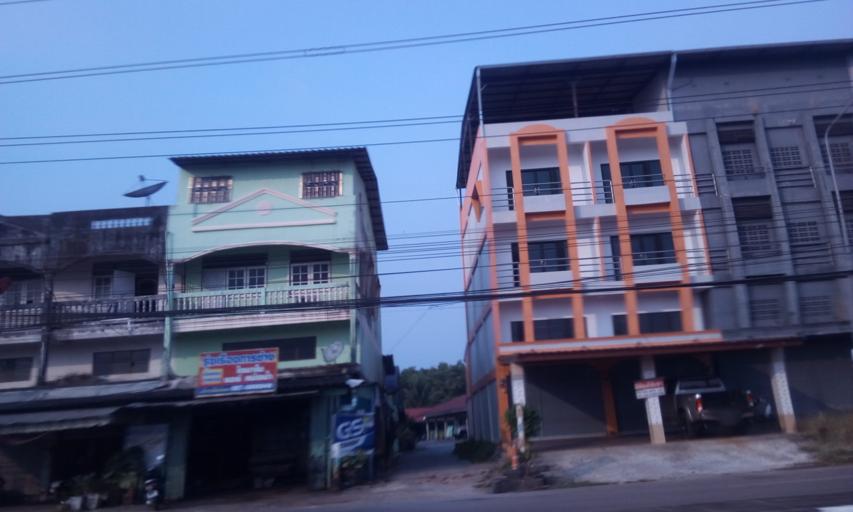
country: TH
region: Trat
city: Khao Saming
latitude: 12.3800
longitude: 102.3759
